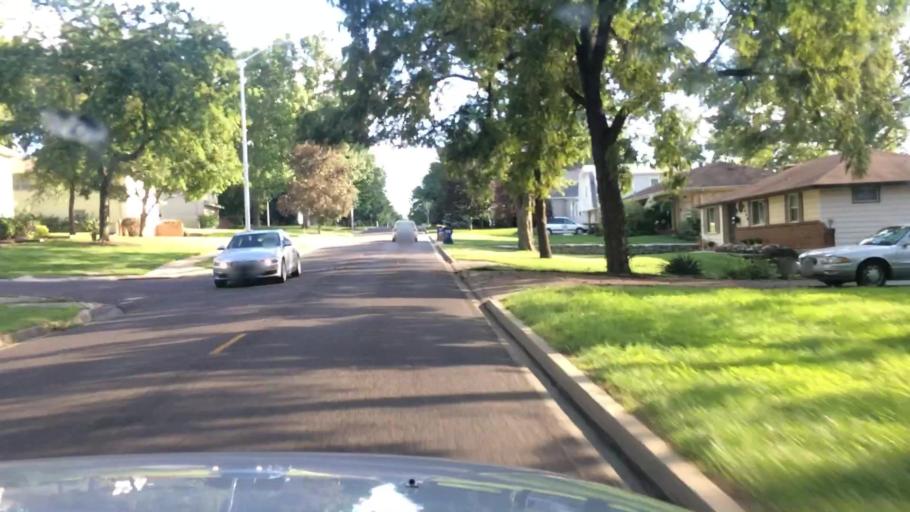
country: US
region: Kansas
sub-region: Johnson County
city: Overland Park
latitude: 38.9746
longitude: -94.6583
